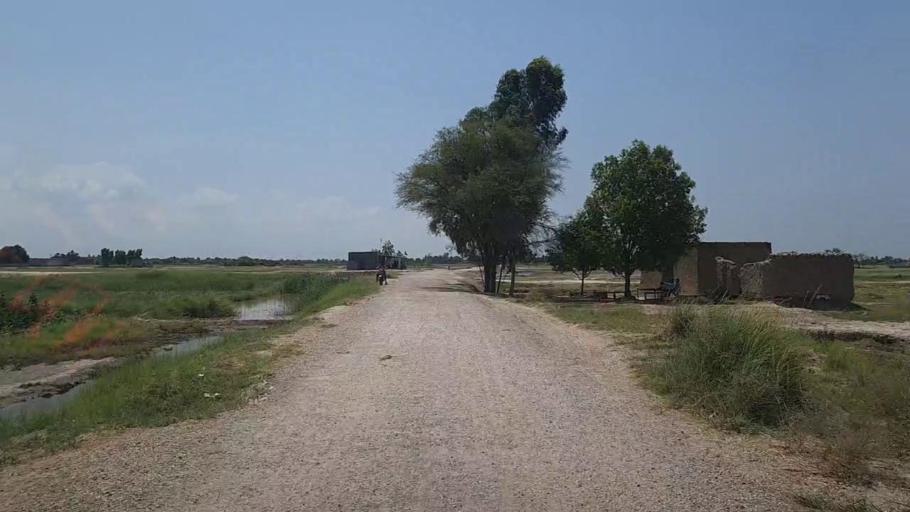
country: PK
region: Sindh
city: Ubauro
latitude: 28.1614
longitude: 69.7644
